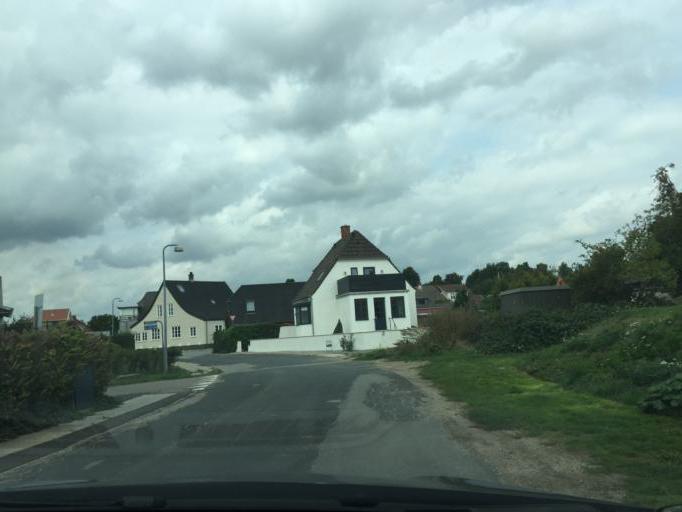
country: DK
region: South Denmark
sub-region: Odense Kommune
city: Stige
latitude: 55.4355
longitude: 10.4165
